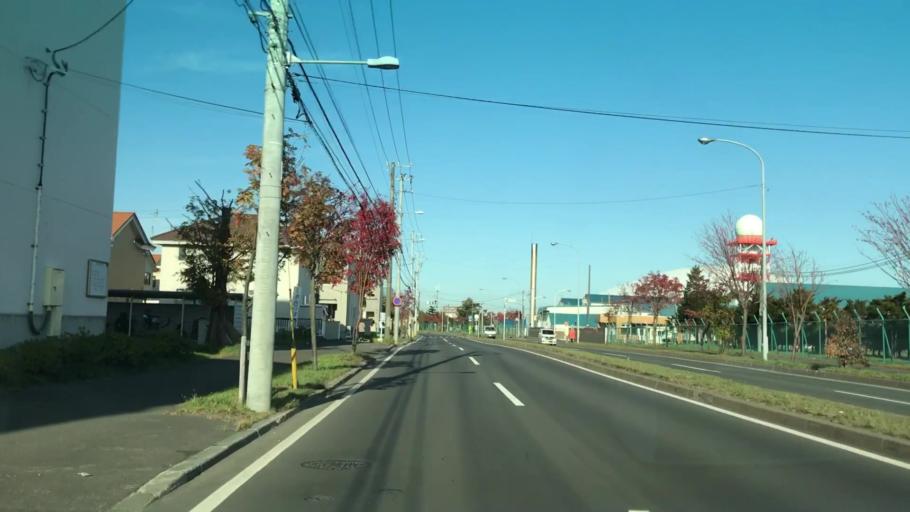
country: JP
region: Hokkaido
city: Sapporo
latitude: 43.1116
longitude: 141.3781
